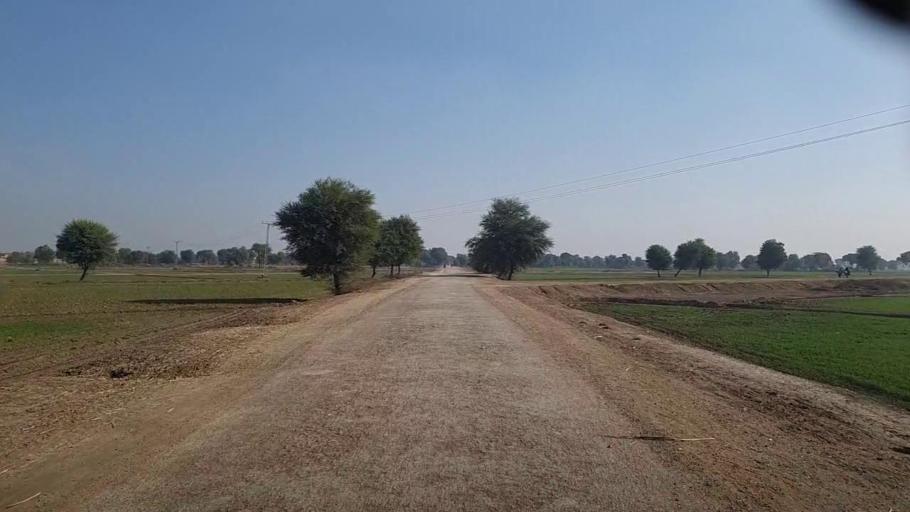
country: PK
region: Sindh
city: Darya Khan Marri
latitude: 26.6663
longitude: 68.3359
